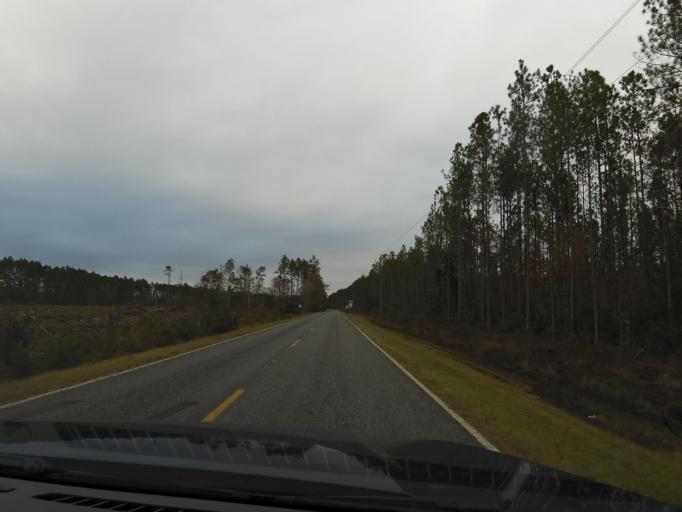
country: US
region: Georgia
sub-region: Charlton County
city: Folkston
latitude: 30.8698
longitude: -82.0428
